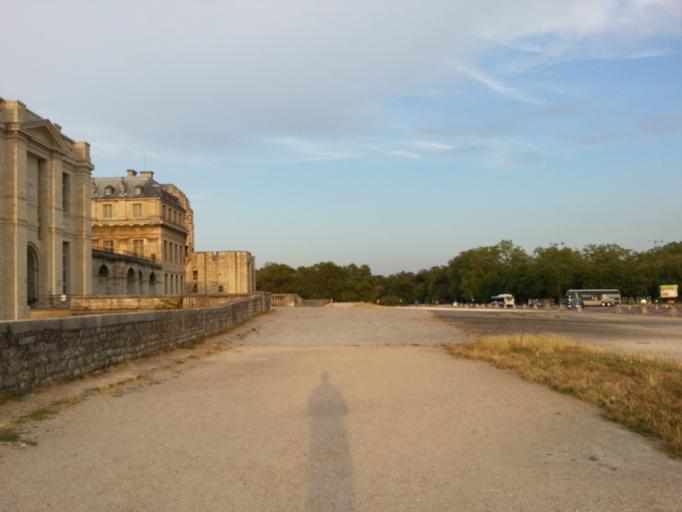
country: FR
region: Ile-de-France
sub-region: Departement du Val-de-Marne
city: Vincennes
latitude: 48.8411
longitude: 2.4351
